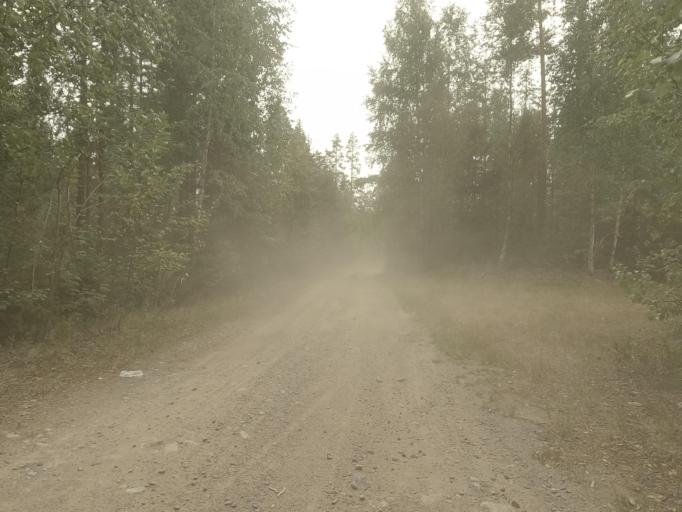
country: RU
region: Leningrad
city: Kamennogorsk
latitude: 61.0109
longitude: 29.2063
